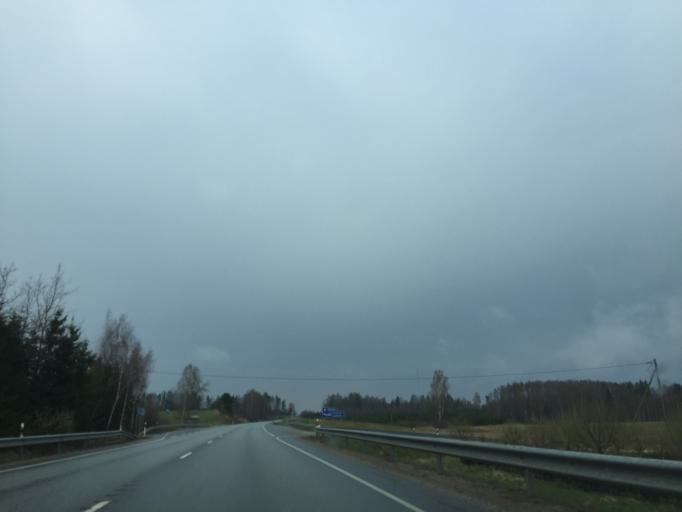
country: EE
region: Tartu
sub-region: UElenurme vald
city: Ulenurme
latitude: 58.1715
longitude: 26.6914
